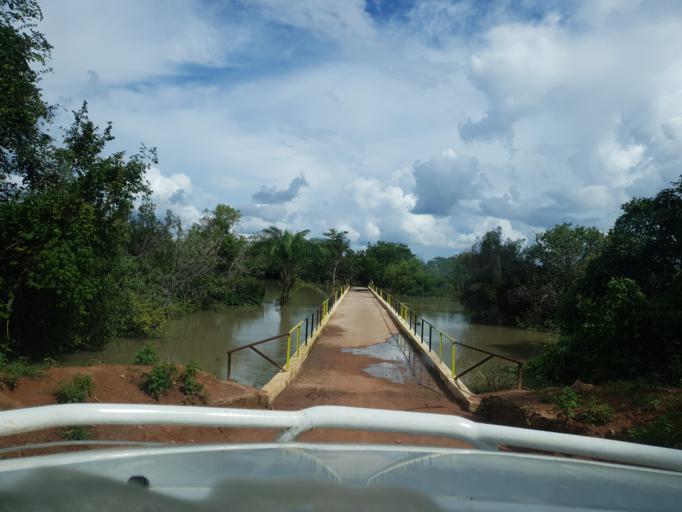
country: CI
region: Savanes
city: Tengrela
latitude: 10.4554
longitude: -6.7951
